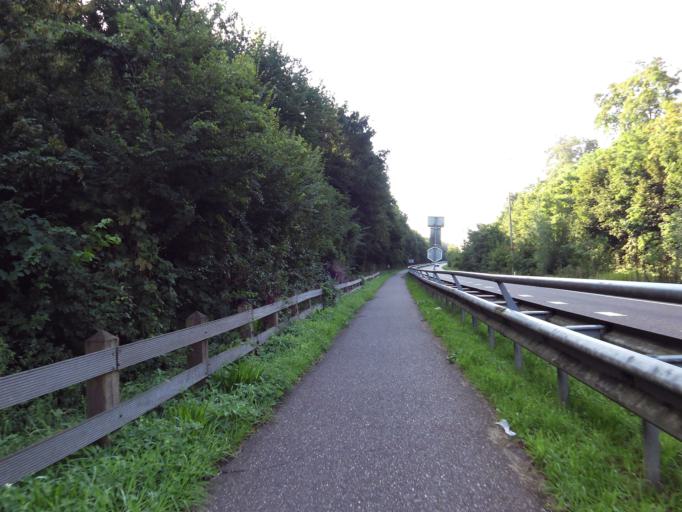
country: NL
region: Limburg
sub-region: Gemeente Kerkrade
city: Kerkrade
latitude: 50.8869
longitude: 6.0536
